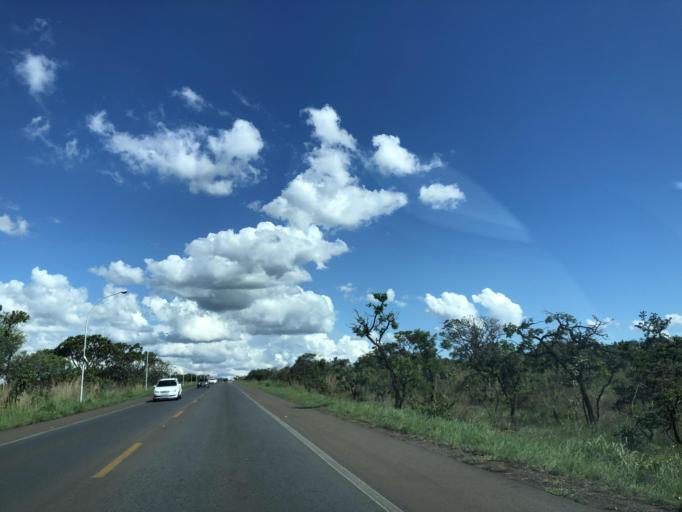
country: BR
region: Federal District
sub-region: Brasilia
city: Brasilia
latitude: -15.6649
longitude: -47.8875
